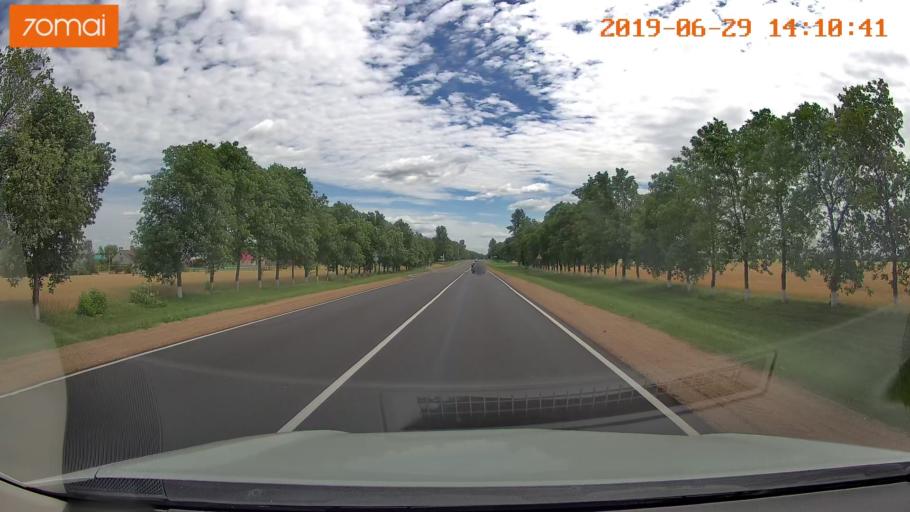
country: BY
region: Minsk
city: Salihorsk
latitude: 52.8255
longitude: 27.4979
